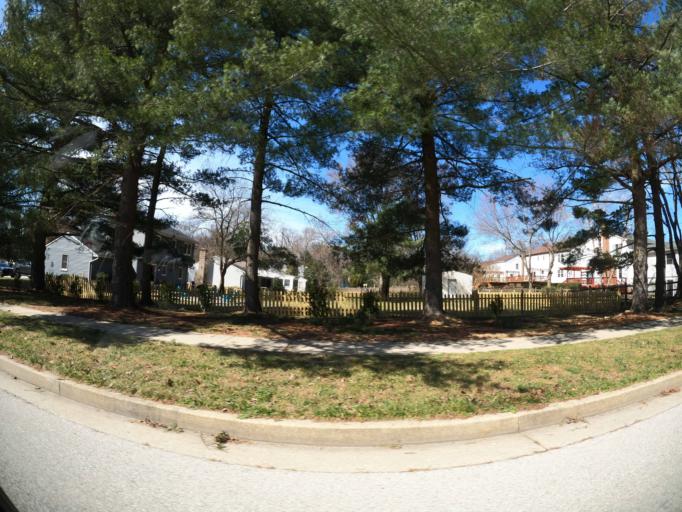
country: US
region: Maryland
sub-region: Howard County
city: Columbia
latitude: 39.2267
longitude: -76.8273
